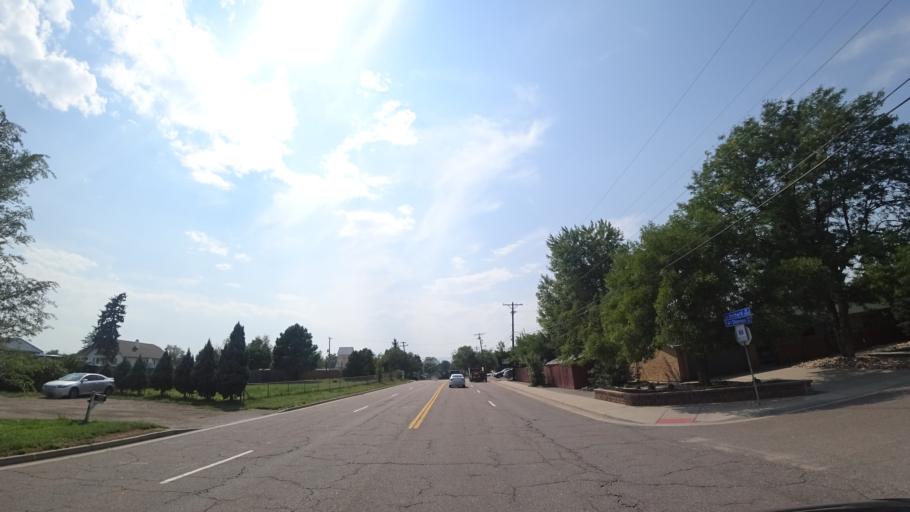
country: US
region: Colorado
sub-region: Arapahoe County
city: Littleton
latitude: 39.6096
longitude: -104.9851
